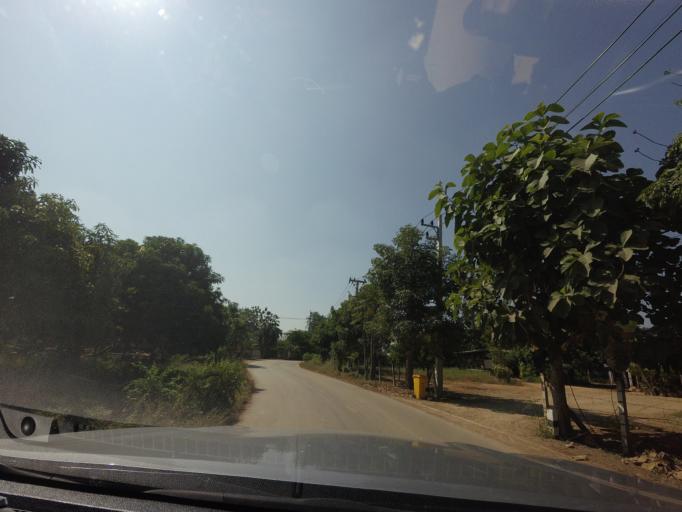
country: TH
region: Sukhothai
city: Si Samrong
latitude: 17.2191
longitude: 99.7750
